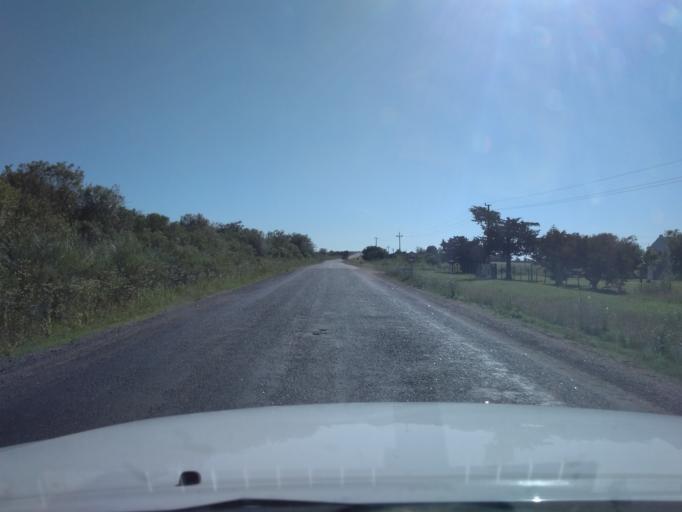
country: UY
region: Canelones
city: San Ramon
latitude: -34.2683
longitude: -55.9358
